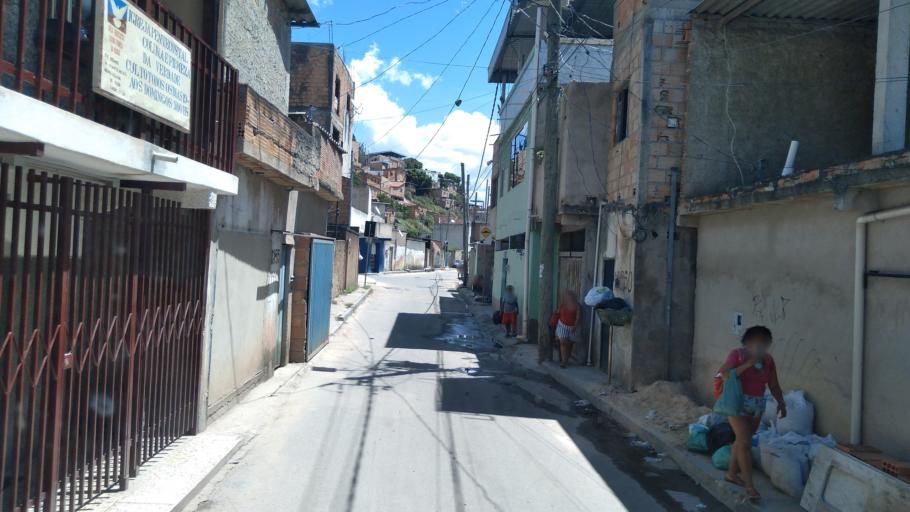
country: BR
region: Minas Gerais
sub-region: Santa Luzia
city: Santa Luzia
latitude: -19.8368
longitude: -43.8957
